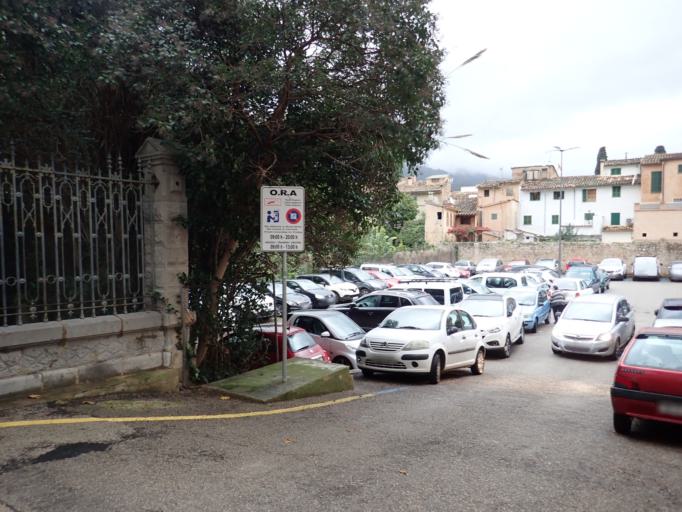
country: ES
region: Balearic Islands
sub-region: Illes Balears
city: Soller
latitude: 39.7663
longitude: 2.7132
